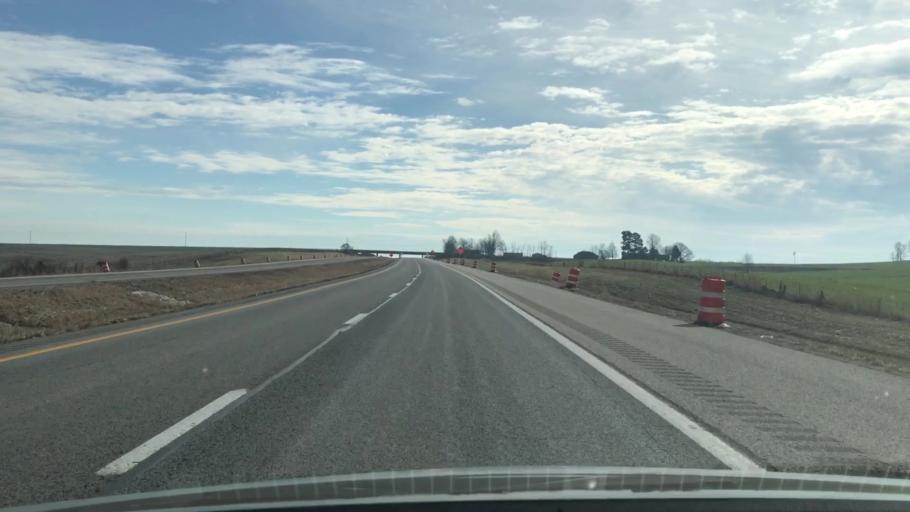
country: US
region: Kentucky
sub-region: Daviess County
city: Masonville
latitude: 37.6659
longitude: -87.0202
